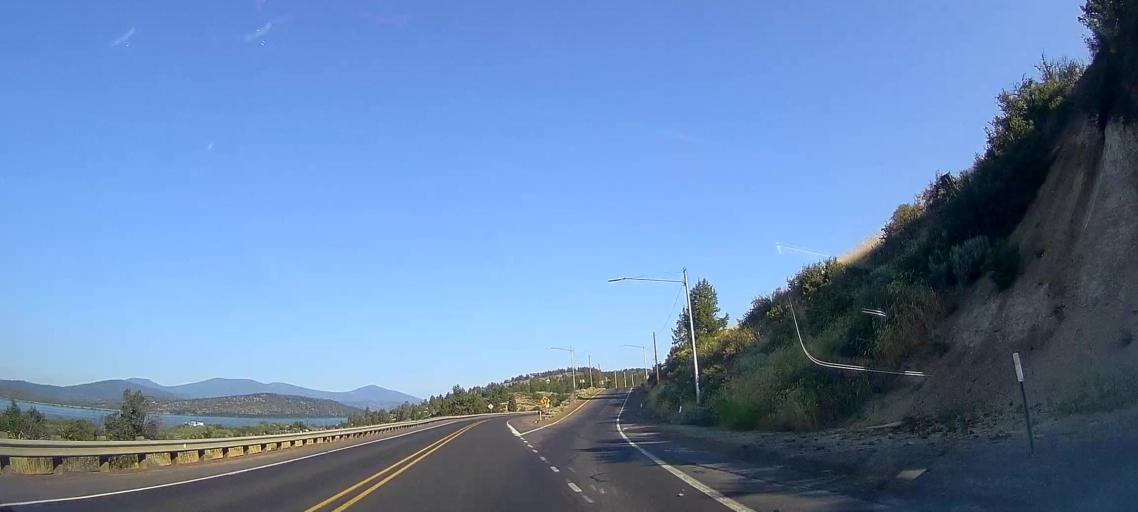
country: US
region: Oregon
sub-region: Klamath County
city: Klamath Falls
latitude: 42.2613
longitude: -121.8072
